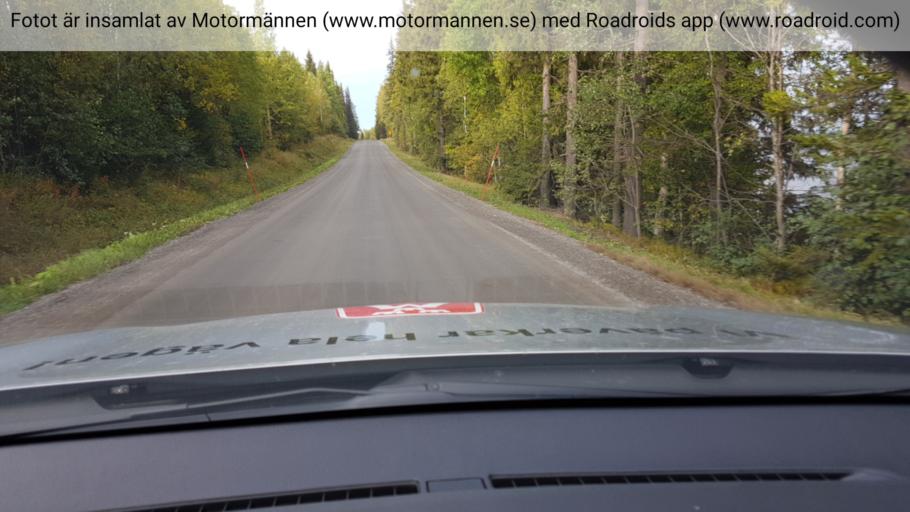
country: SE
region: Jaemtland
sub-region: Stroemsunds Kommun
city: Stroemsund
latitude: 63.9983
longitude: 15.8165
